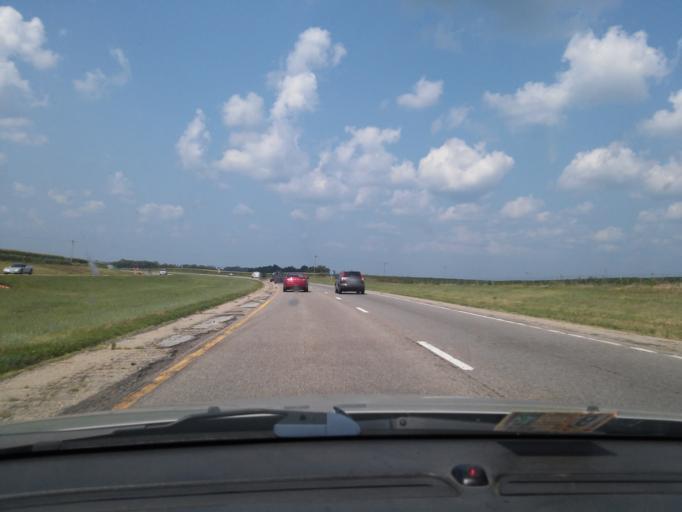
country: US
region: Illinois
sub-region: Logan County
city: Atlanta
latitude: 40.2649
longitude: -89.2146
